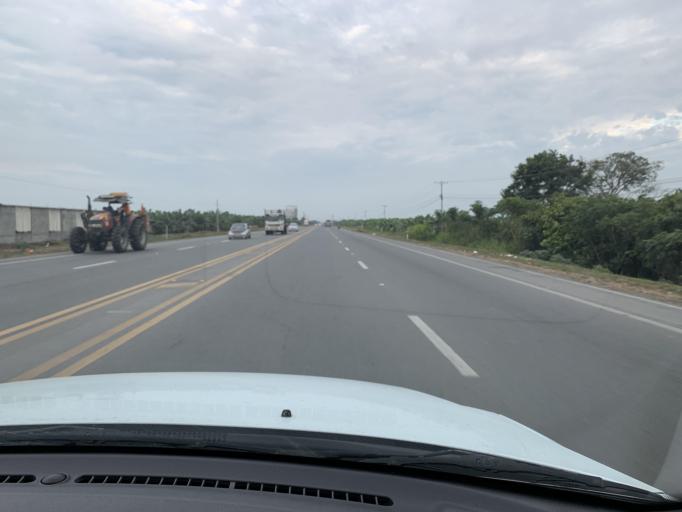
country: EC
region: Guayas
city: Yaguachi Nuevo
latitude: -2.2544
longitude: -79.6236
